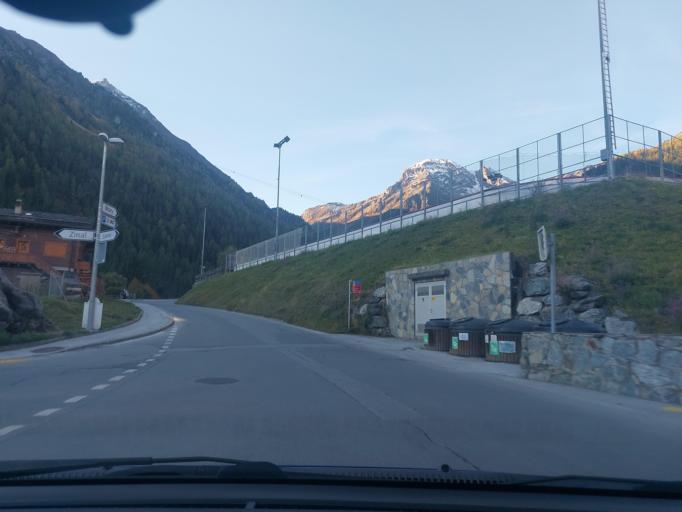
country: CH
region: Valais
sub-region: Herens District
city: Evolene
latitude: 46.1783
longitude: 7.5760
